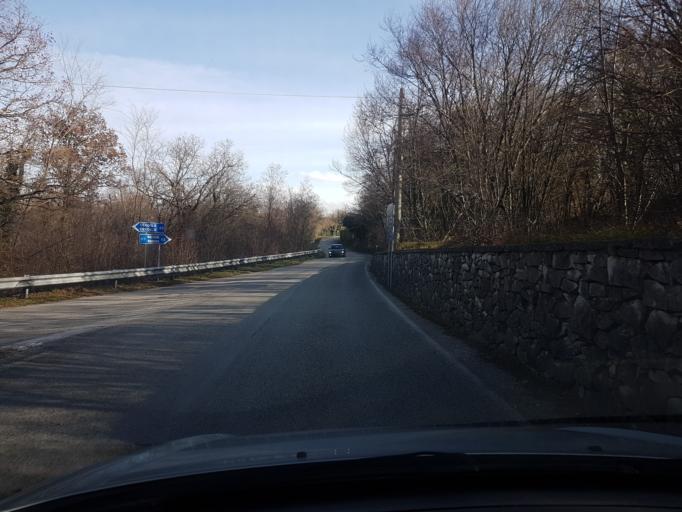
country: IT
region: Friuli Venezia Giulia
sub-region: Provincia di Trieste
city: Sistiana-Visogliano
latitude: 45.7857
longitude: 13.6545
